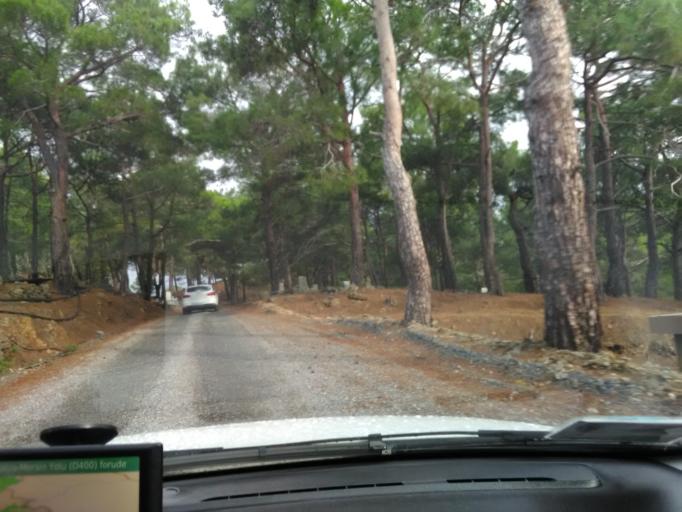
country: TR
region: Antalya
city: Gazipasa
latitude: 36.1573
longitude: 32.4293
